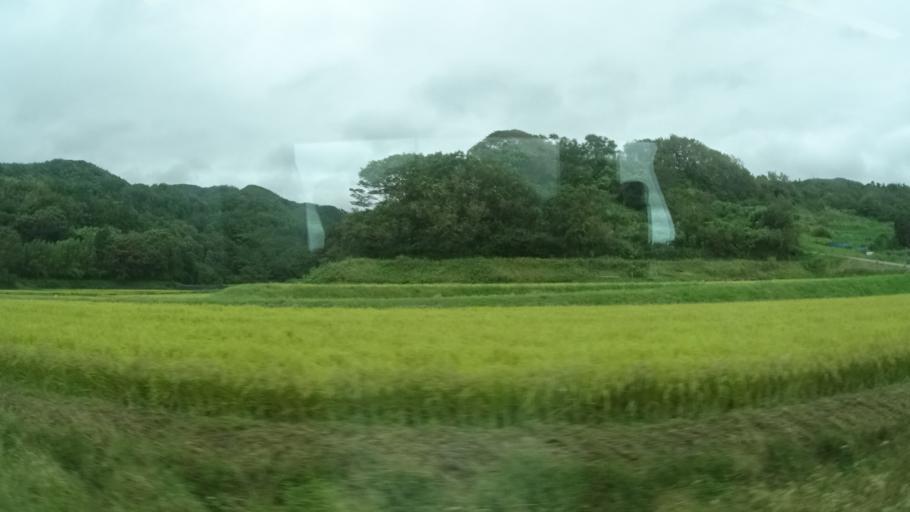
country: JP
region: Niigata
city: Murakami
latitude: 38.2908
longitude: 139.4506
